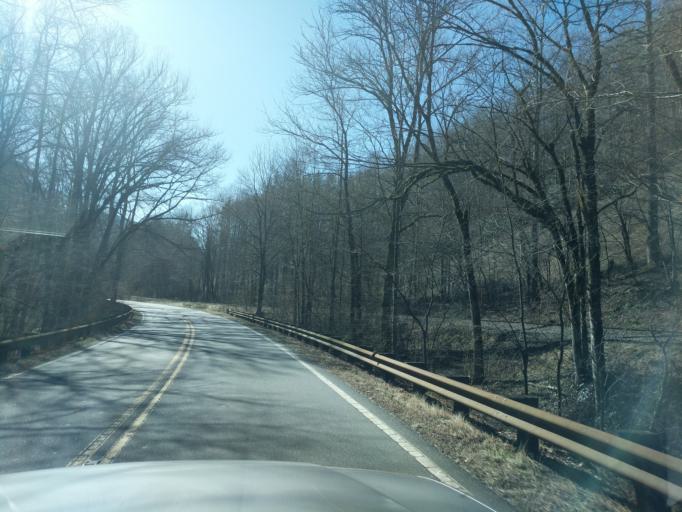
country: US
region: North Carolina
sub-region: Graham County
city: Robbinsville
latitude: 35.2950
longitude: -83.6610
